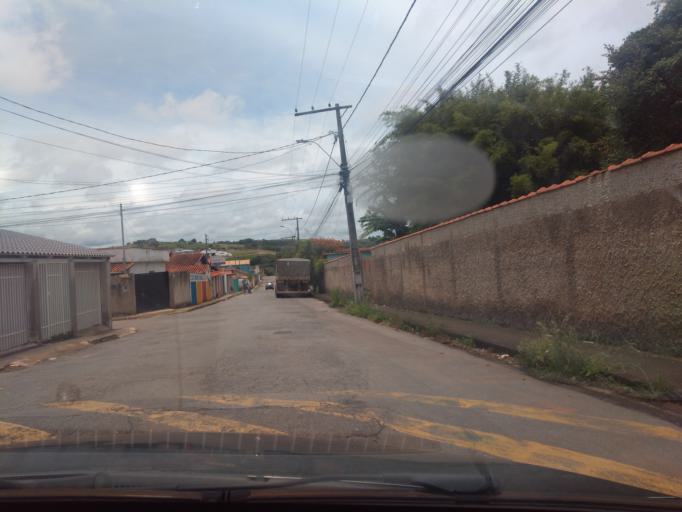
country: BR
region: Minas Gerais
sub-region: Tres Coracoes
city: Tres Coracoes
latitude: -21.6826
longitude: -45.2601
